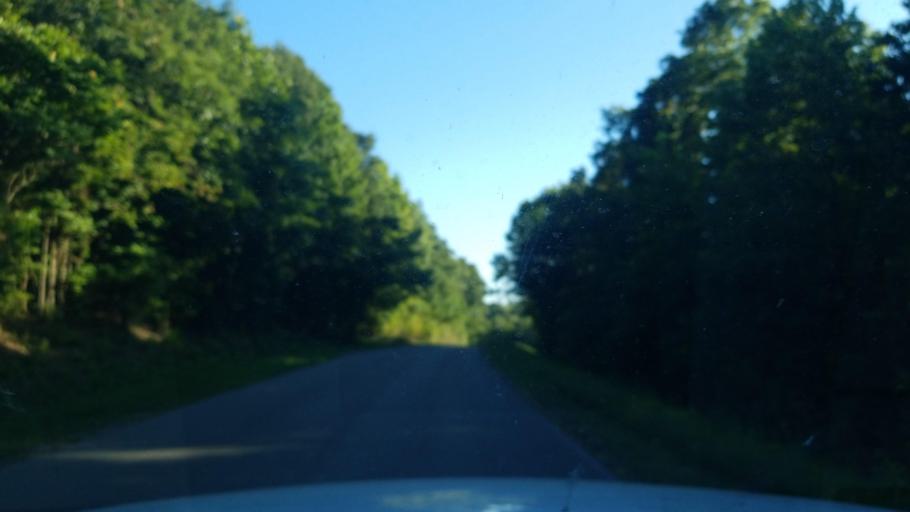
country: US
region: Illinois
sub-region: Hardin County
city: Elizabethtown
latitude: 37.5929
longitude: -88.3651
